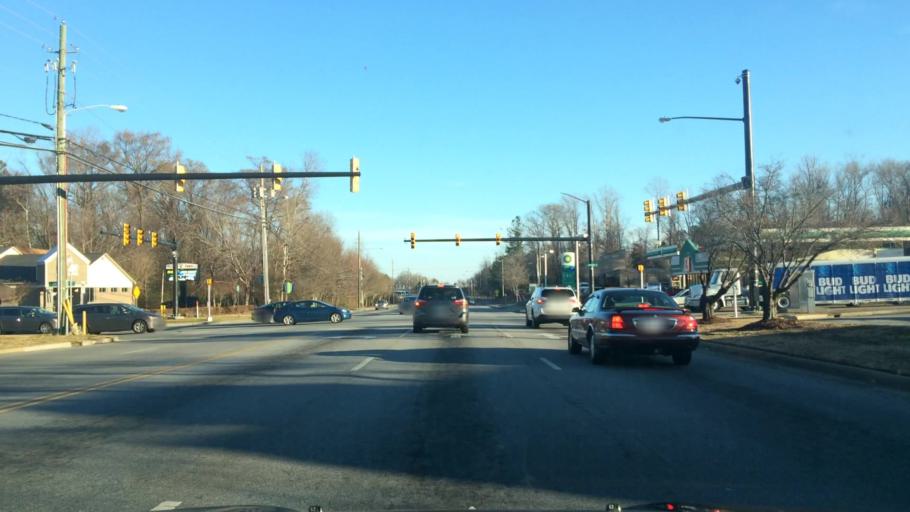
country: US
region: North Carolina
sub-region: Pitt County
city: Greenville
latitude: 35.5905
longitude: -77.3783
